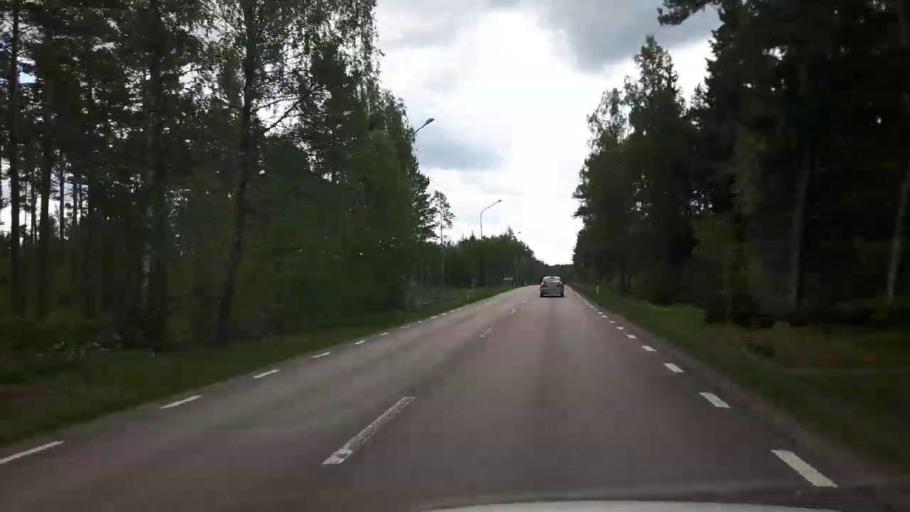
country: SE
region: Dalarna
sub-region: Faluns Kommun
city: Falun
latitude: 60.5162
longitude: 15.7352
